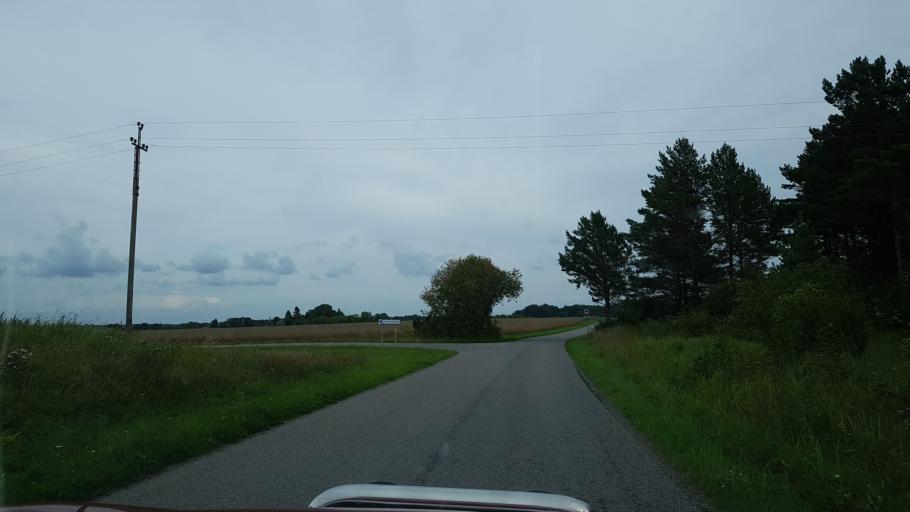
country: EE
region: Laeaene
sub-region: Ridala Parish
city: Uuemoisa
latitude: 58.9986
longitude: 23.7439
